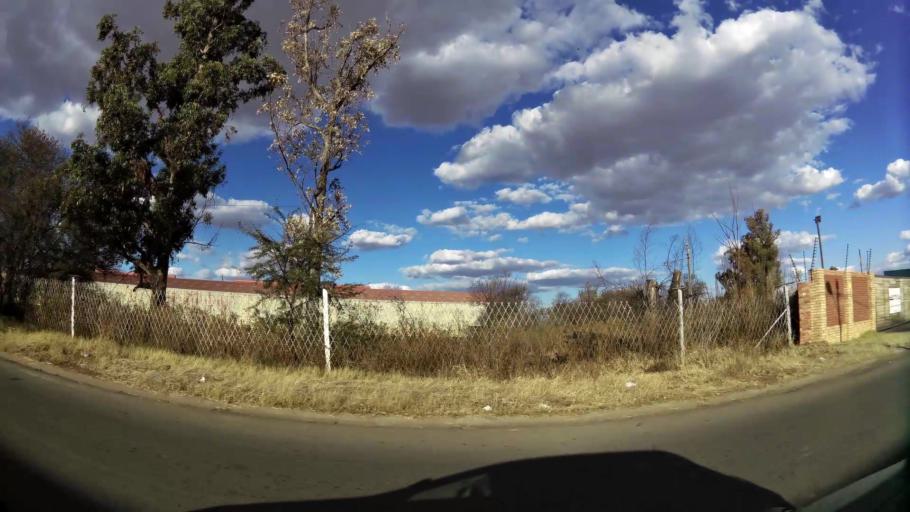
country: ZA
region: North-West
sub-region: Dr Kenneth Kaunda District Municipality
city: Potchefstroom
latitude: -26.7120
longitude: 27.0812
